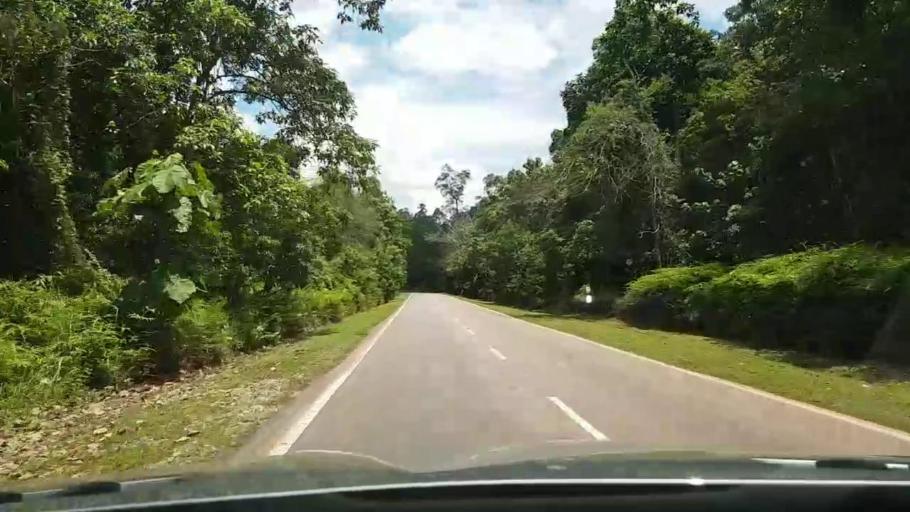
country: MY
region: Pahang
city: Pekan
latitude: 3.1475
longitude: 102.9704
